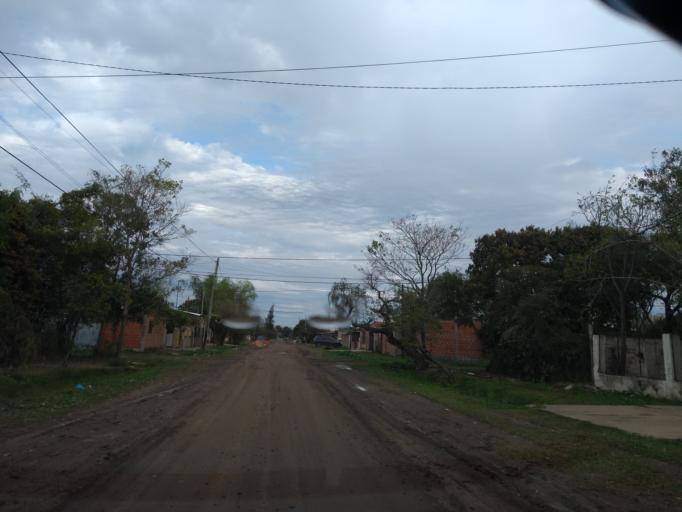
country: AR
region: Chaco
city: Resistencia
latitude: -27.4778
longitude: -58.9785
